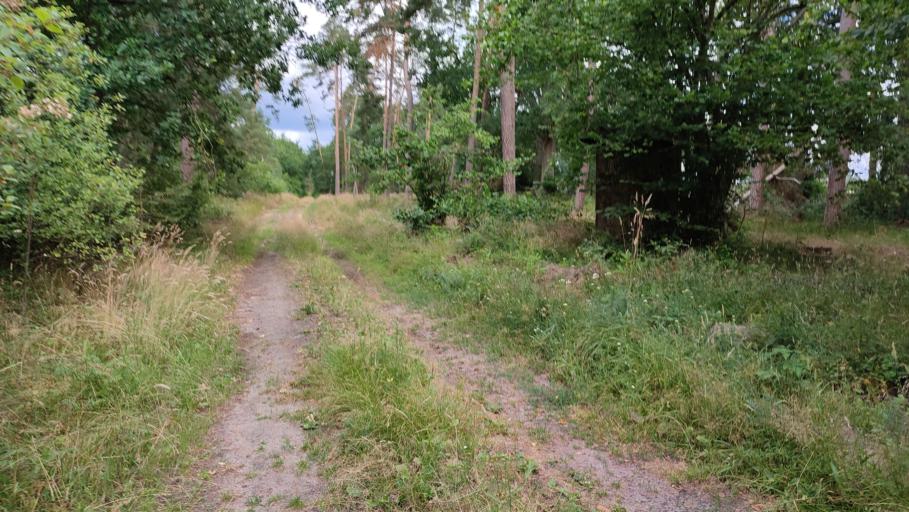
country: DE
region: Lower Saxony
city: Hitzacker
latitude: 53.1955
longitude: 11.0953
